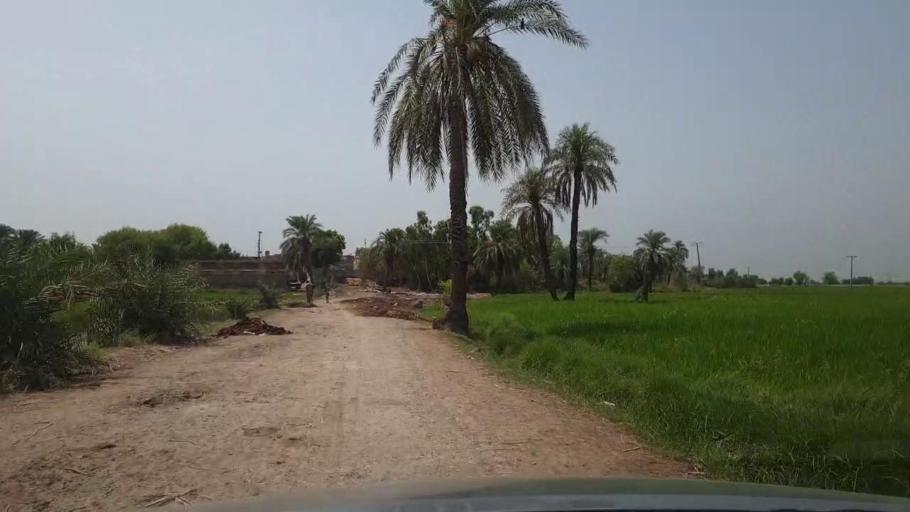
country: PK
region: Sindh
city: Madeji
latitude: 27.7877
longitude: 68.4339
